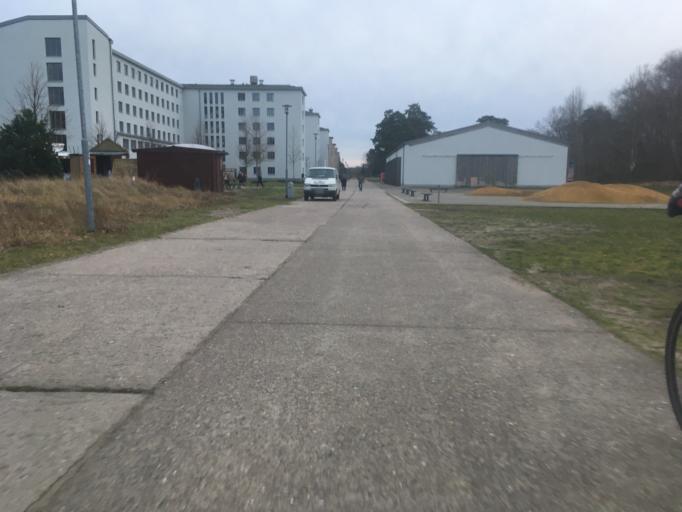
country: DE
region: Mecklenburg-Vorpommern
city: Ostseebad Binz
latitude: 54.4524
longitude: 13.5688
